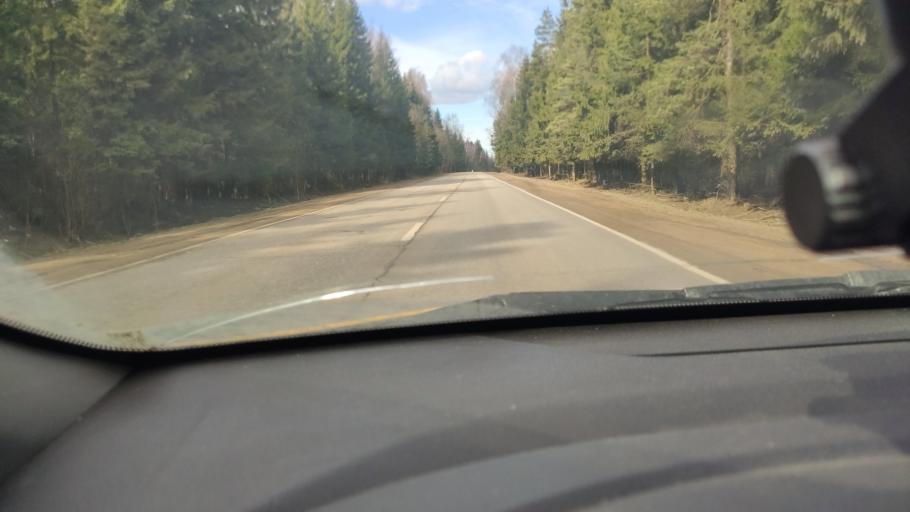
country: RU
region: Moskovskaya
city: Ruza
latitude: 55.7199
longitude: 36.1642
